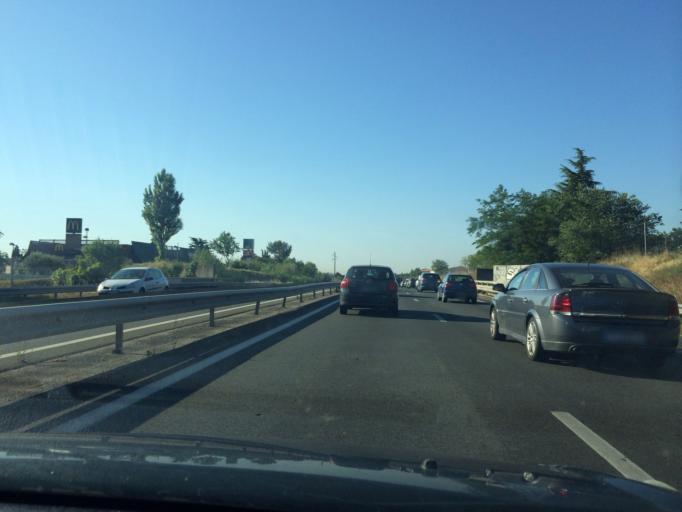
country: FR
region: Languedoc-Roussillon
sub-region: Departement de l'Herault
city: Juvignac
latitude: 43.6145
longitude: 3.7991
